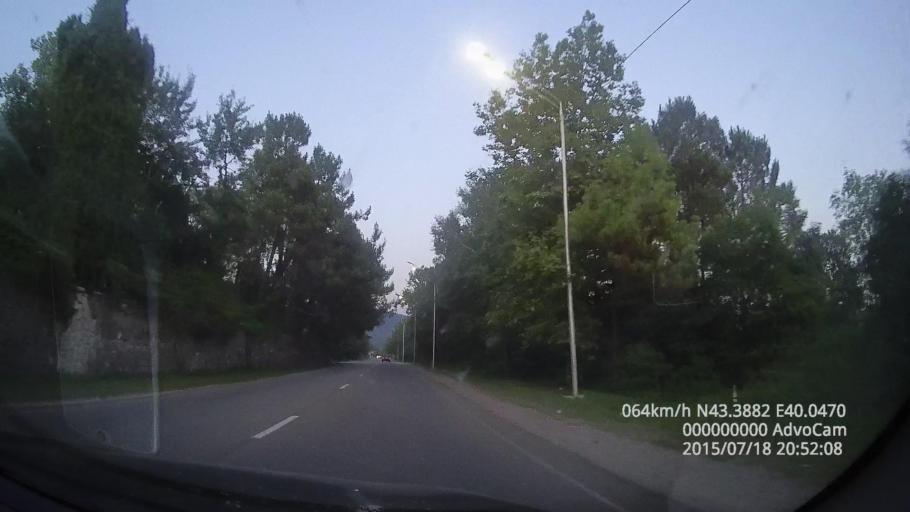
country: GE
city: Gantiadi
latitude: 43.3880
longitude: 40.0485
